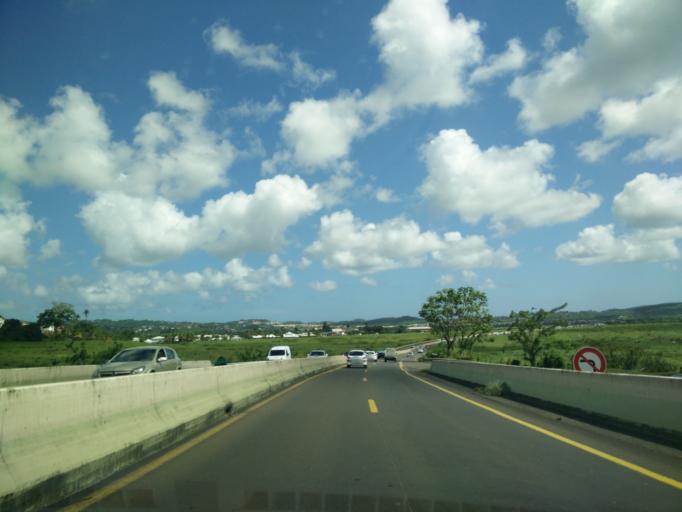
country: MQ
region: Martinique
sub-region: Martinique
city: Ducos
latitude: 14.5538
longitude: -60.9713
